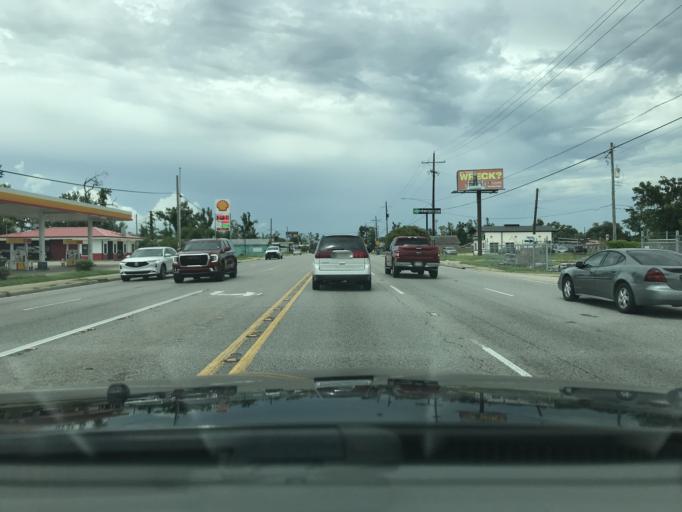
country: US
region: Louisiana
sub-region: Calcasieu Parish
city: Moss Bluff
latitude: 30.2571
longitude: -93.1806
